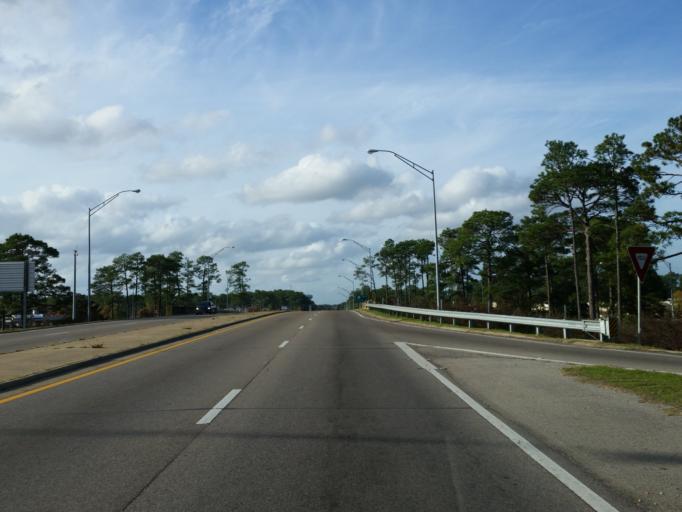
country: US
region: Mississippi
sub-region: Forrest County
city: Hattiesburg
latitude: 31.3067
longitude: -89.3159
